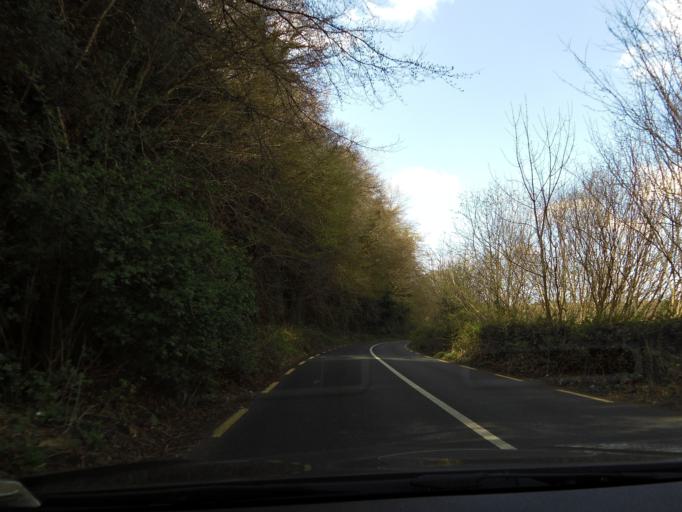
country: IE
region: Leinster
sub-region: Wicklow
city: Arklow
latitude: 52.8273
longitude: -6.2231
